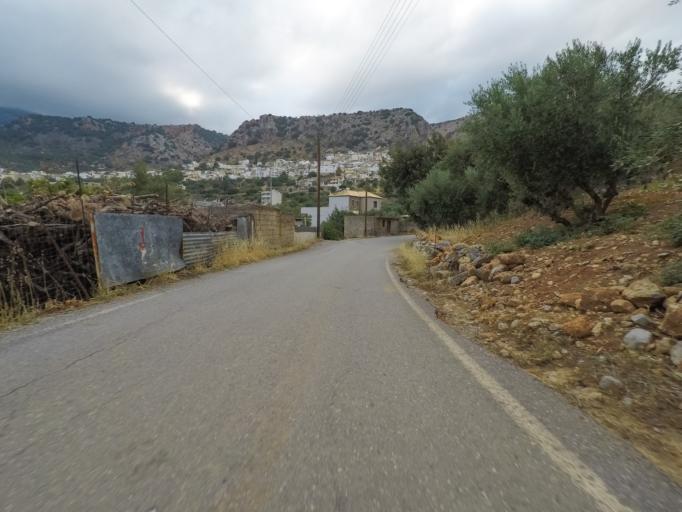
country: GR
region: Crete
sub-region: Nomos Lasithiou
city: Kritsa
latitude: 35.1603
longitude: 25.6495
